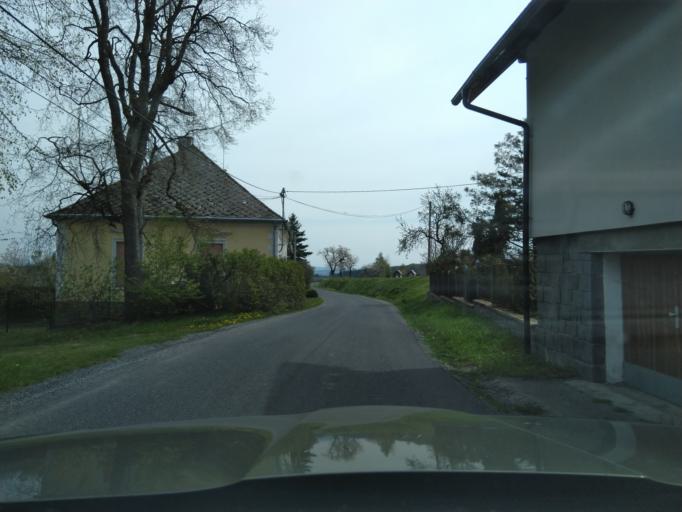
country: CZ
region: Jihocesky
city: Vacov
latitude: 49.1735
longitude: 13.6779
